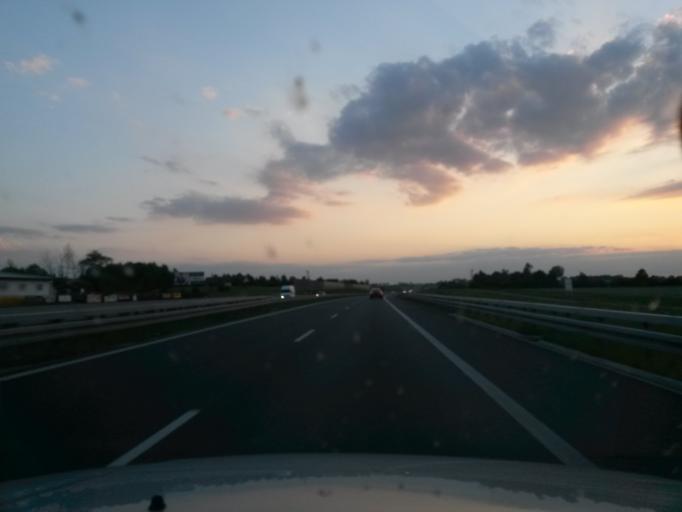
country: PL
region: Lower Silesian Voivodeship
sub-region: Powiat olesnicki
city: Sycow
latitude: 51.2938
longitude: 17.7140
